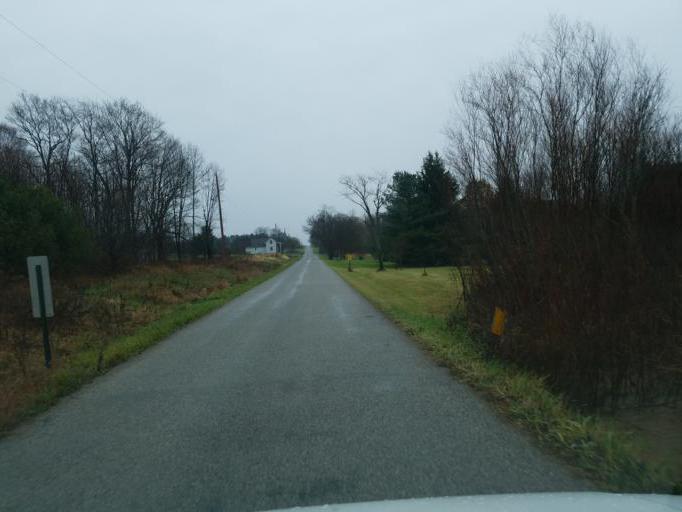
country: US
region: Ohio
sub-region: Knox County
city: Centerburg
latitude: 40.3621
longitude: -82.6861
